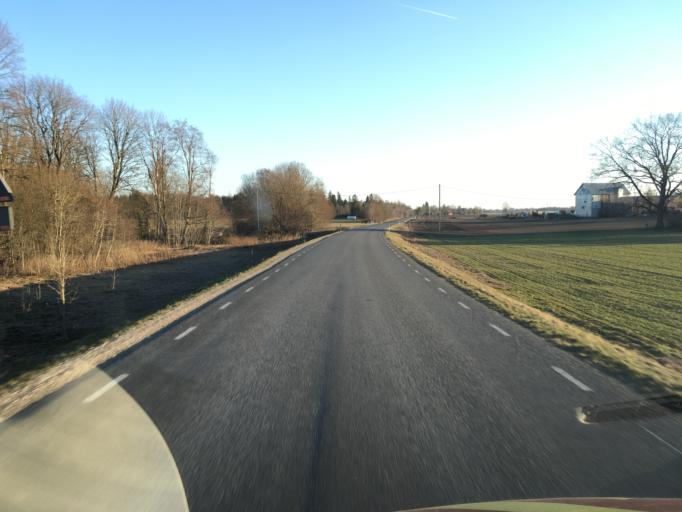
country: EE
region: Raplamaa
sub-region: Kehtna vald
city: Kehtna
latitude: 59.0519
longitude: 24.9497
